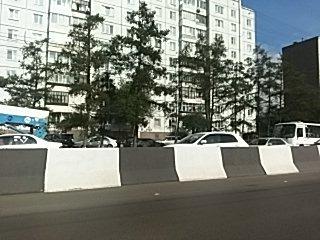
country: RU
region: Krasnoyarskiy
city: Solnechnyy
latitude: 56.0445
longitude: 92.9444
